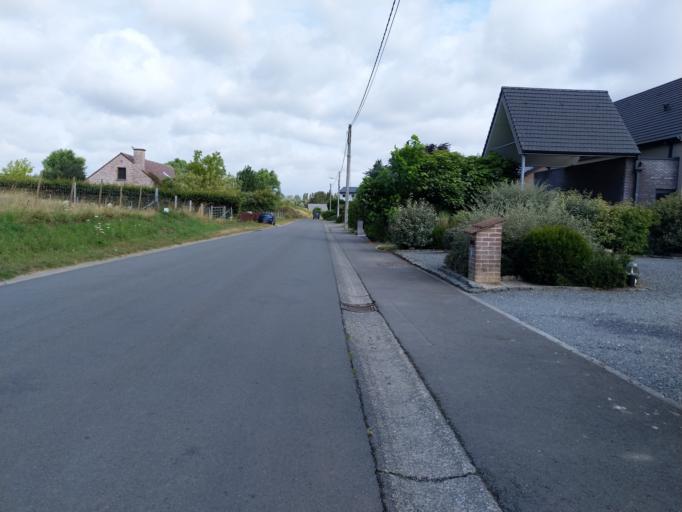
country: BE
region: Wallonia
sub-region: Province du Hainaut
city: Chievres
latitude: 50.5947
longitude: 3.8044
